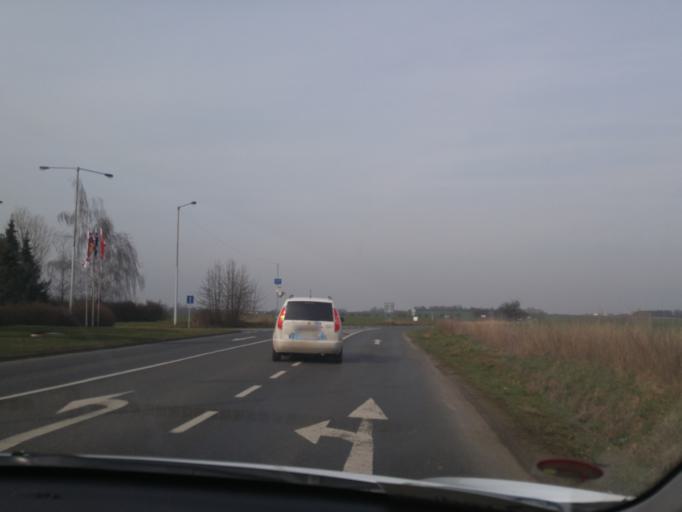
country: CZ
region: Central Bohemia
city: Brandys nad Labem-Stara Boleslav
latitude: 50.1910
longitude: 14.6471
